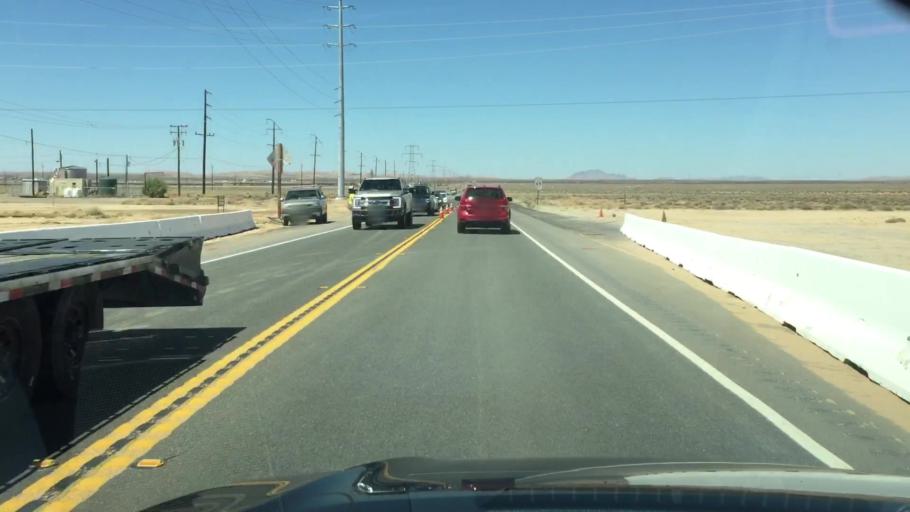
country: US
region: California
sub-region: Kern County
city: Boron
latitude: 34.9976
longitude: -117.5430
